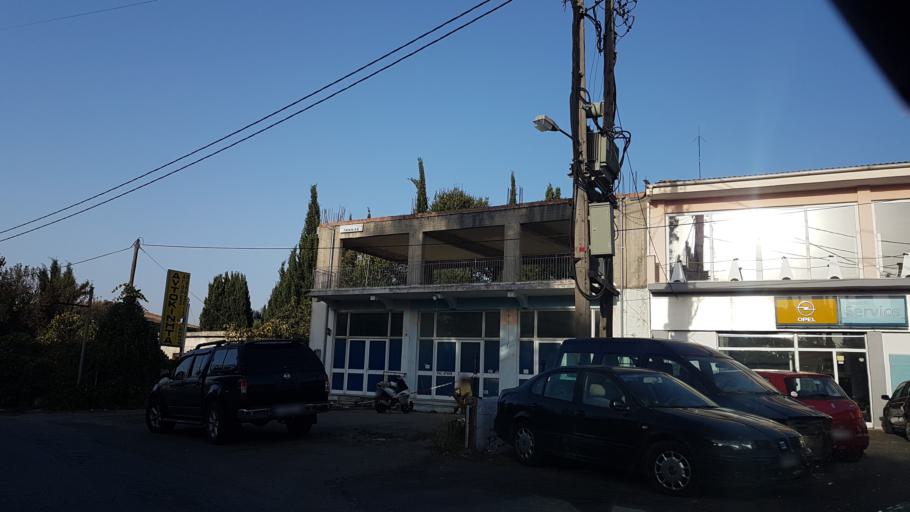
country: GR
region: Ionian Islands
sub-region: Nomos Kerkyras
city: Kanali
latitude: 39.6028
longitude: 19.8951
